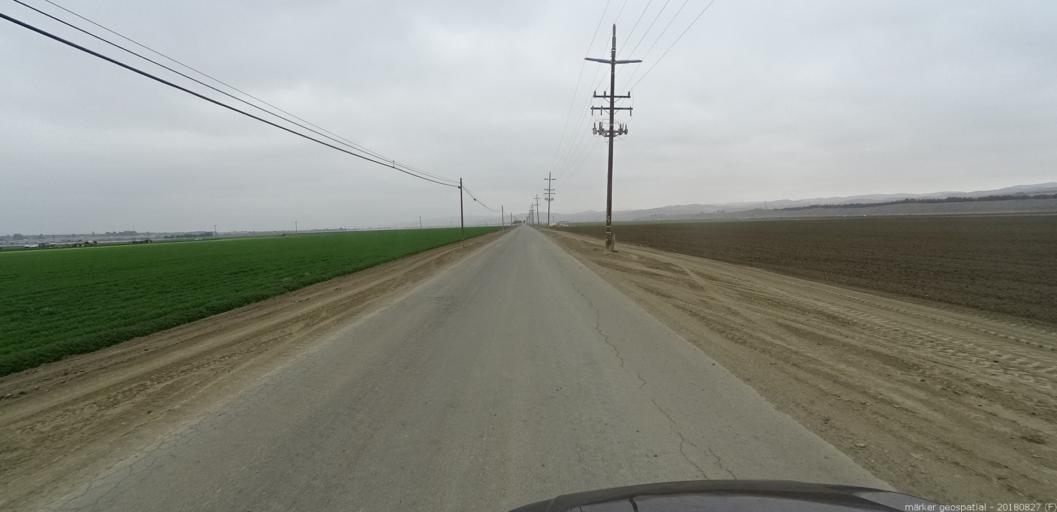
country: US
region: California
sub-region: Monterey County
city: King City
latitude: 36.2502
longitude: -121.1492
